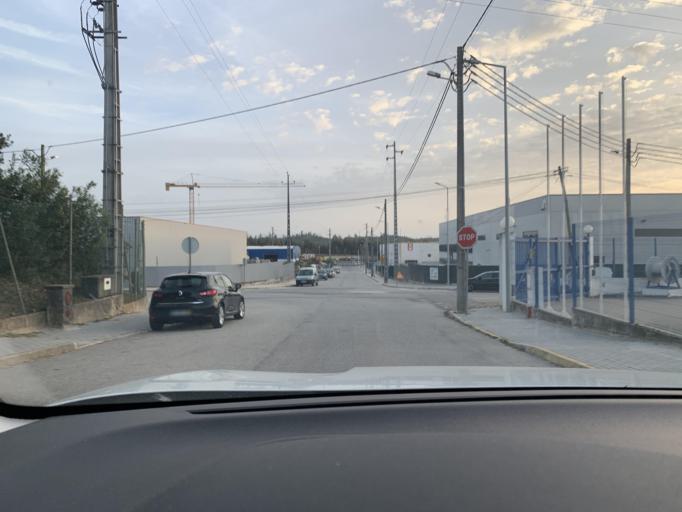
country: PT
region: Viseu
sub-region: Concelho de Tondela
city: Tondela
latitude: 40.4846
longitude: -8.0939
